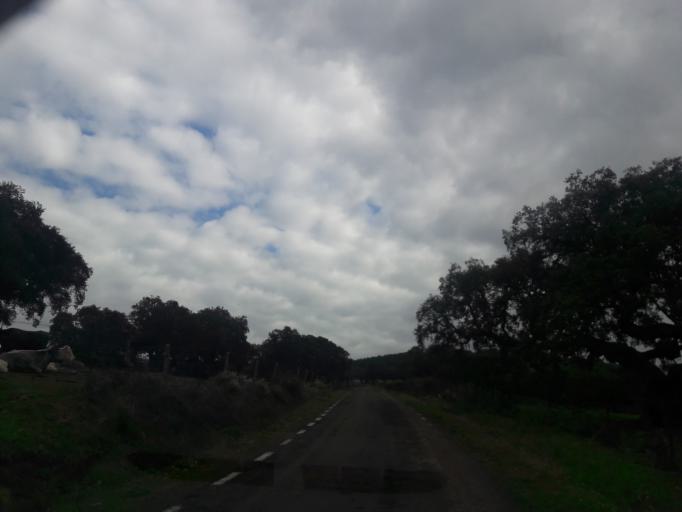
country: ES
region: Castille and Leon
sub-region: Provincia de Salamanca
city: Serradilla del Arroyo
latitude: 40.5078
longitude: -6.4054
